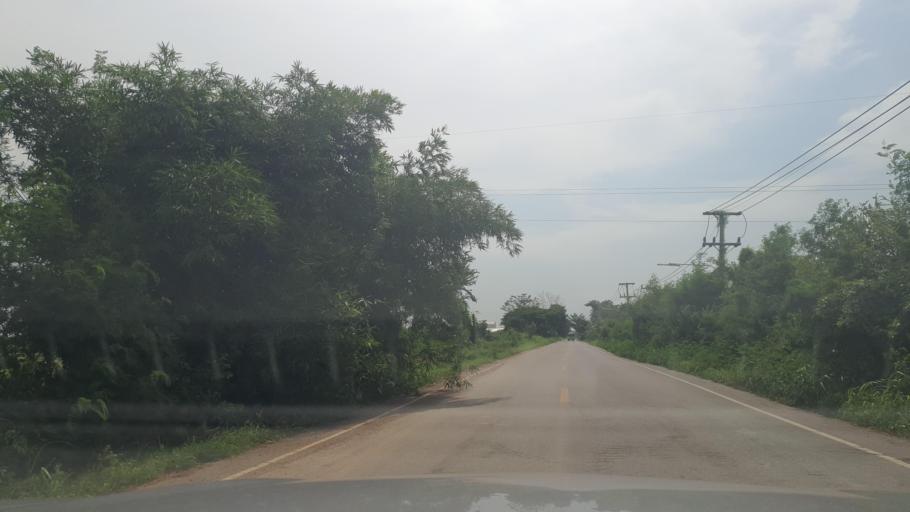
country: TH
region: Sukhothai
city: Si Samrong
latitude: 17.1182
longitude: 99.8710
